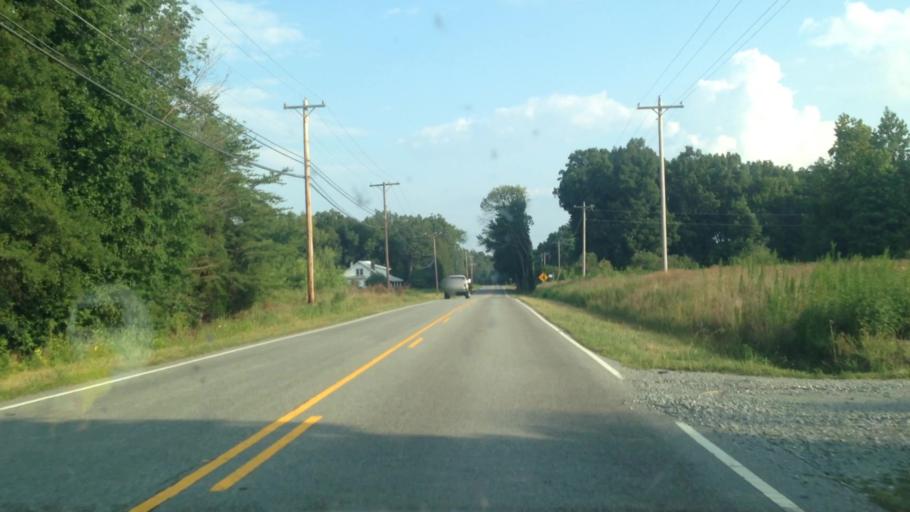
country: US
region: North Carolina
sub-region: Guilford County
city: High Point
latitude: 35.9980
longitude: -80.0630
